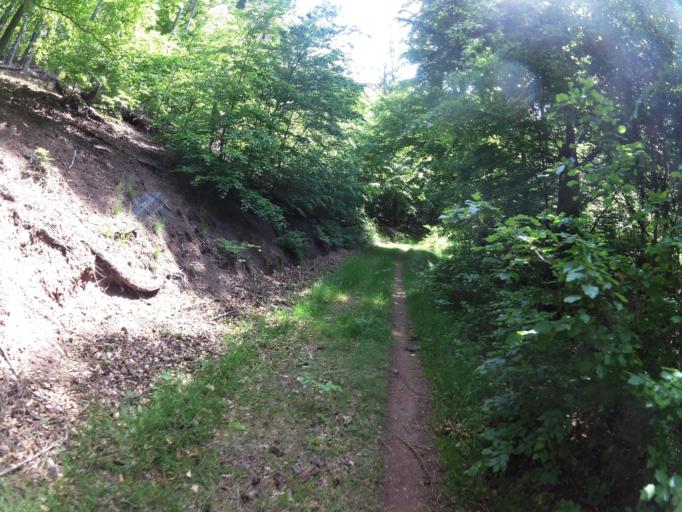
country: DE
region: Thuringia
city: Wolfsburg-Unkeroda
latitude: 50.9501
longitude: 10.2952
